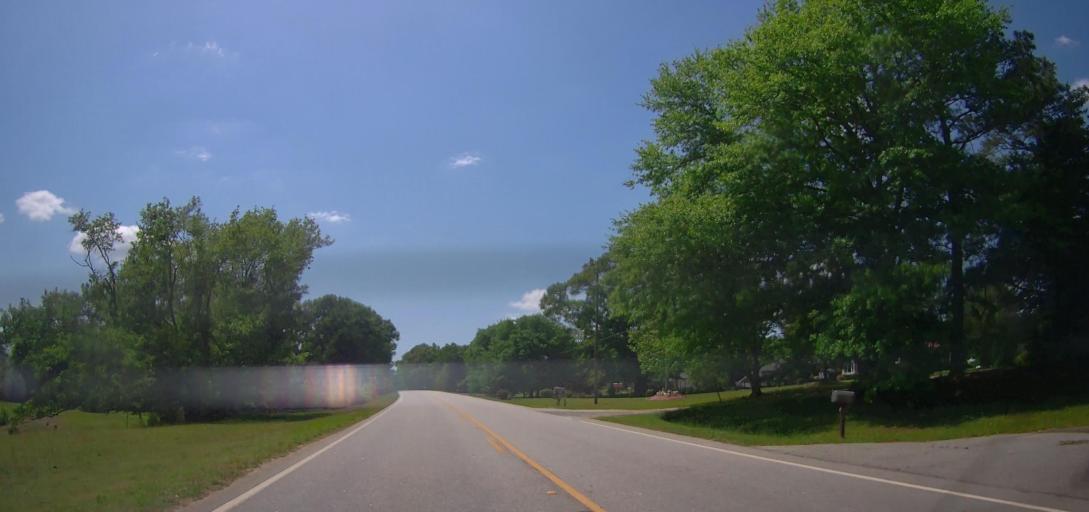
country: US
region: Georgia
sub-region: Putnam County
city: Eatonton
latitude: 33.3400
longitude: -83.3549
